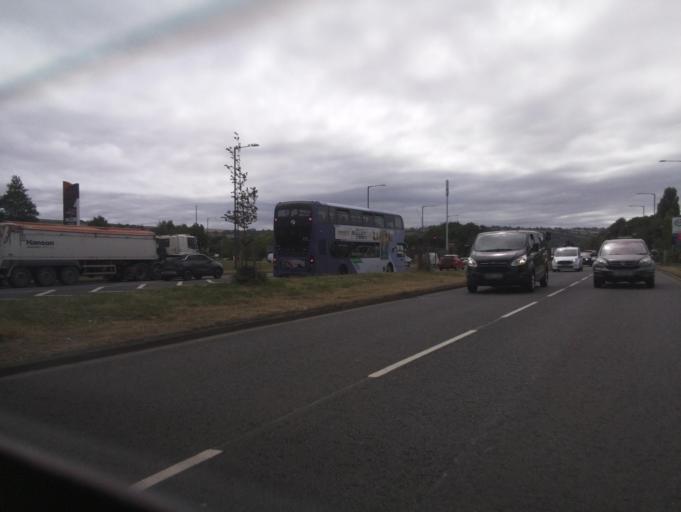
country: GB
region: England
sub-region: Bath and North East Somerset
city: Whitchurch
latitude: 51.4186
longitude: -2.5879
